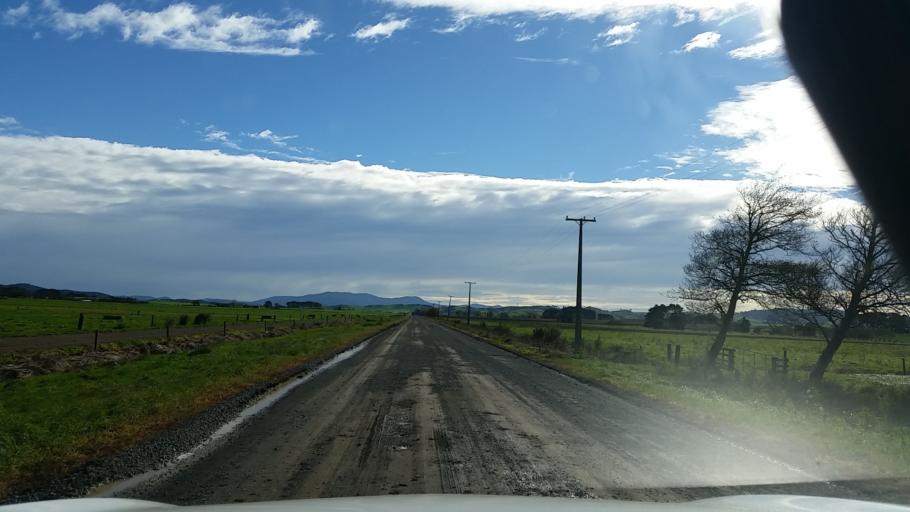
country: NZ
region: Waikato
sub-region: Hamilton City
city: Hamilton
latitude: -37.6418
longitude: 175.4316
